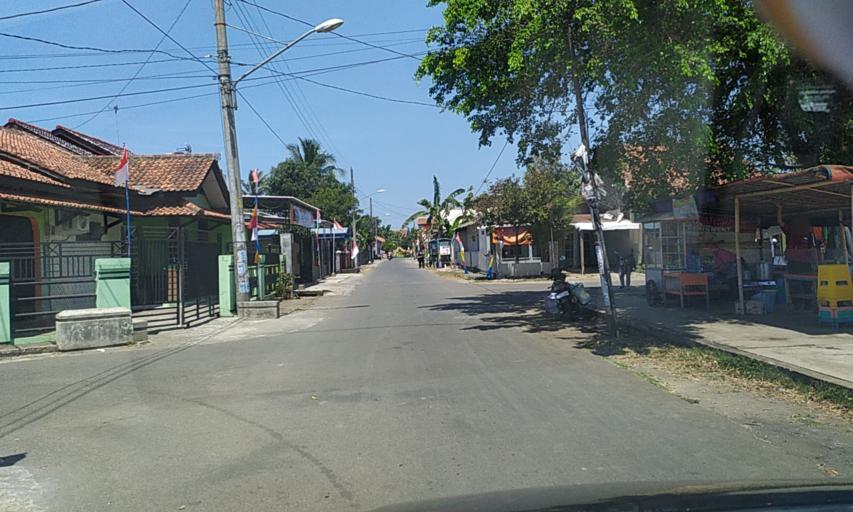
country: ID
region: Central Java
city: Rejanegara
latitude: -7.6775
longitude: 109.0591
